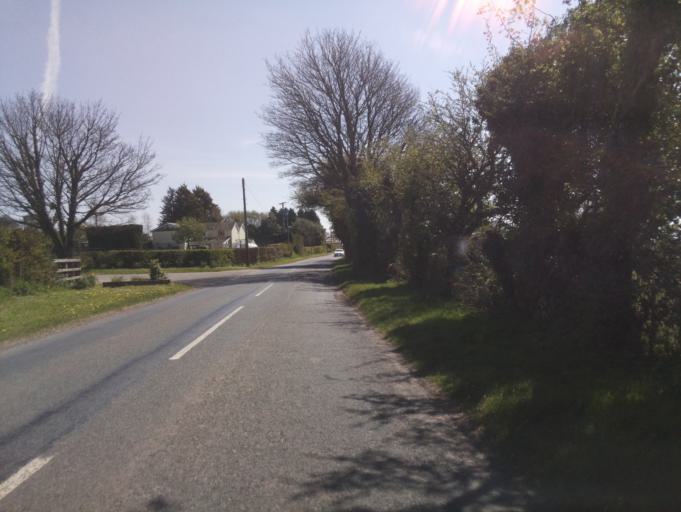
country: GB
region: Wales
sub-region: Newport
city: Llanvaches
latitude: 51.6534
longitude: -2.7842
